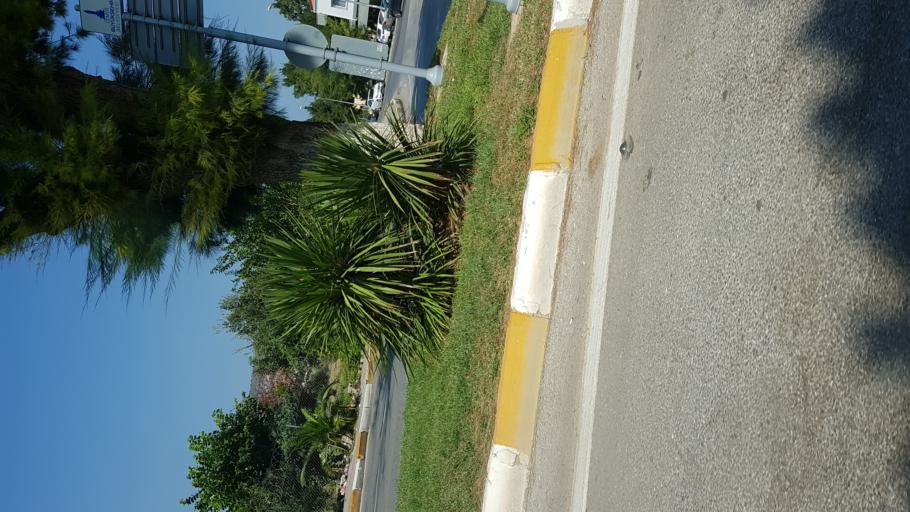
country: TR
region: Izmir
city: Urla
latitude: 38.3618
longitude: 26.7719
